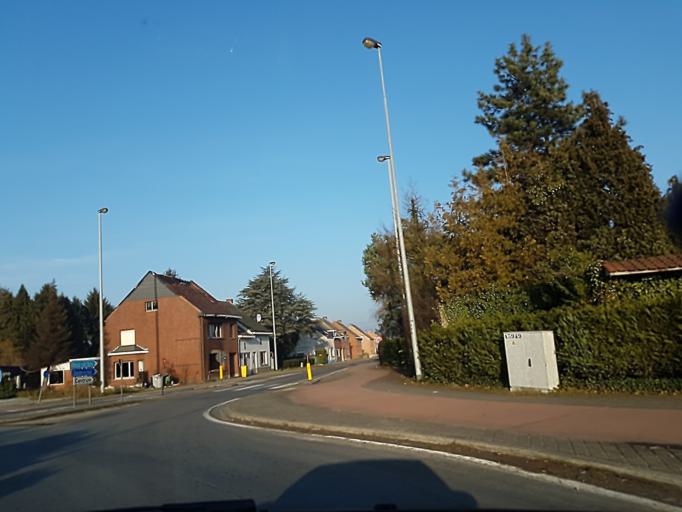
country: BE
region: Flanders
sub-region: Provincie Antwerpen
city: Heist-op-den-Berg
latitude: 51.0525
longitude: 4.7294
